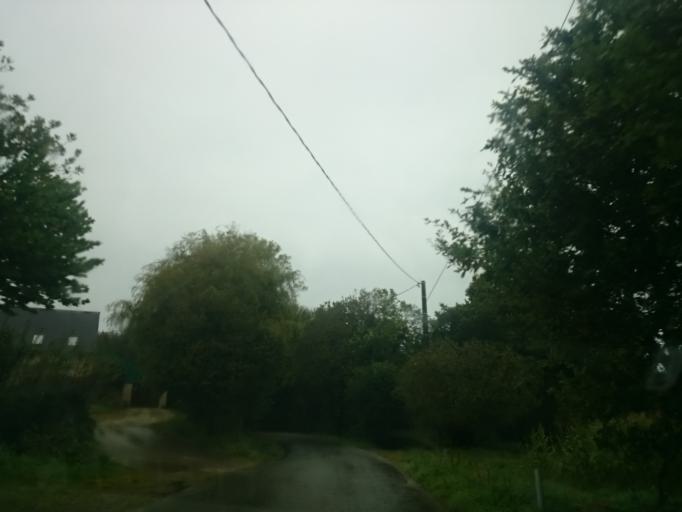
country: FR
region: Brittany
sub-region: Departement du Finistere
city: Kernilis
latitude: 48.5546
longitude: -4.3973
